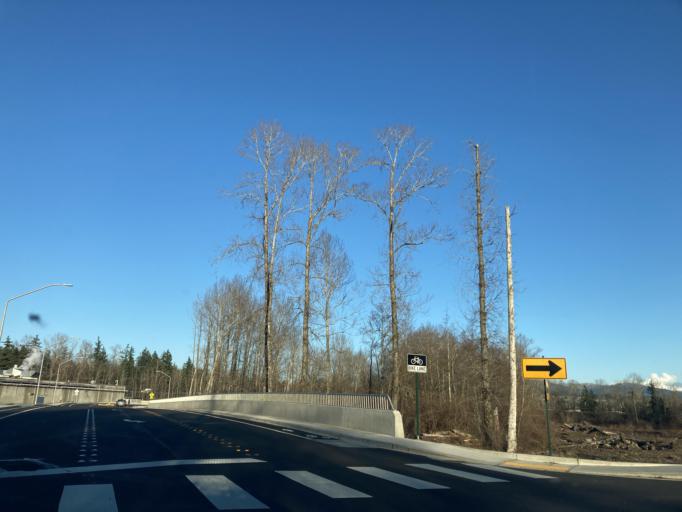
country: US
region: Washington
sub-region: Whatcom County
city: Bellingham
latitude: 48.7771
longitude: -122.4756
